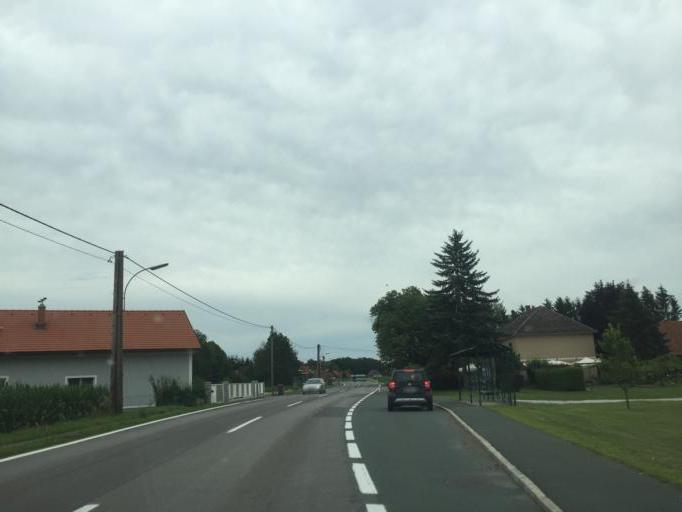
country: AT
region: Styria
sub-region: Politischer Bezirk Leibnitz
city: Spielfeld
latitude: 46.7165
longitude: 15.6752
